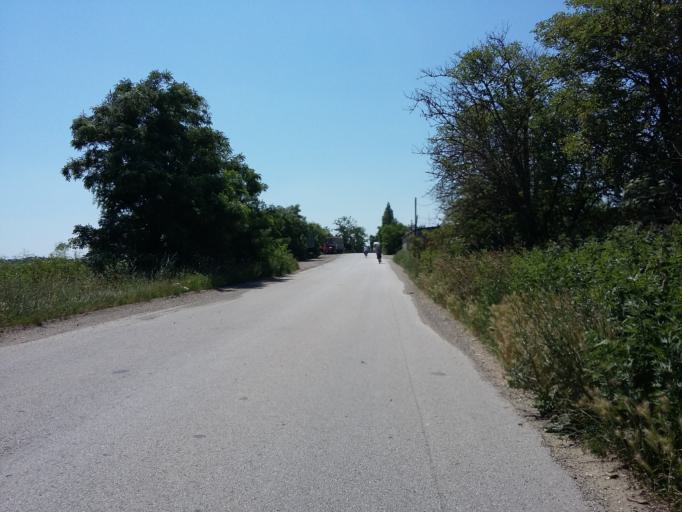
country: AT
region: Lower Austria
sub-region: Politischer Bezirk Ganserndorf
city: Marchegg
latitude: 48.2964
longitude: 16.9681
